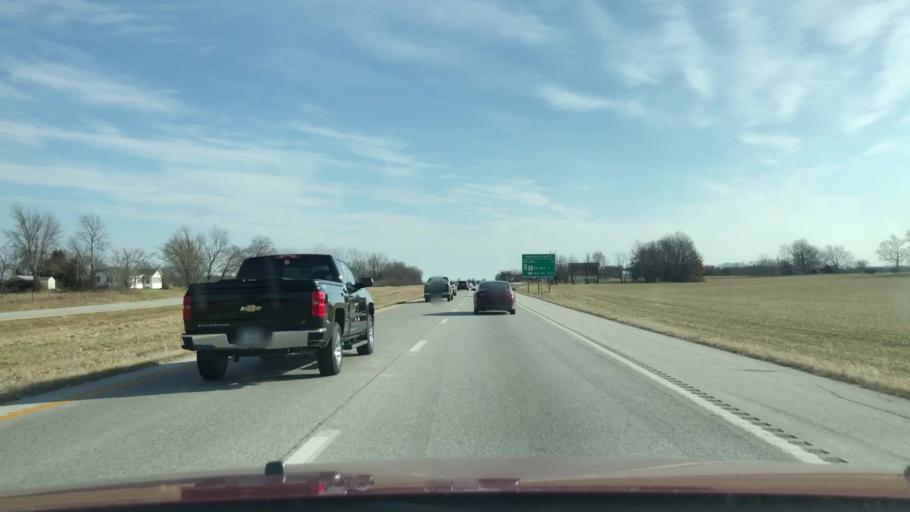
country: US
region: Missouri
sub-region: Webster County
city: Rogersville
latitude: 37.1183
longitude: -93.1047
